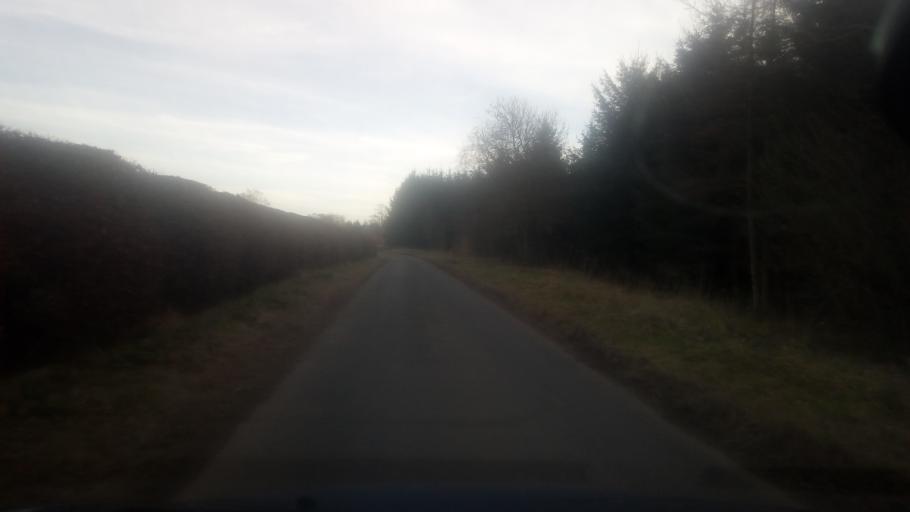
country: GB
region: Scotland
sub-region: The Scottish Borders
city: Jedburgh
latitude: 55.4169
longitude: -2.6185
